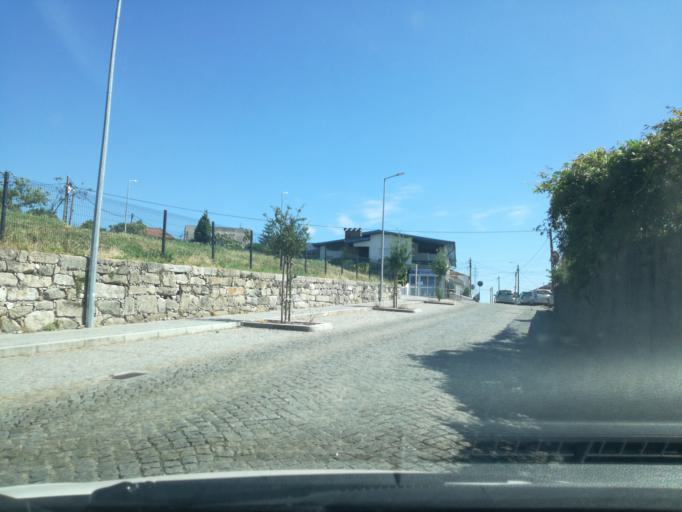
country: PT
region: Porto
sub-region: Maia
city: Anta
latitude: 41.2733
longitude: -8.6334
